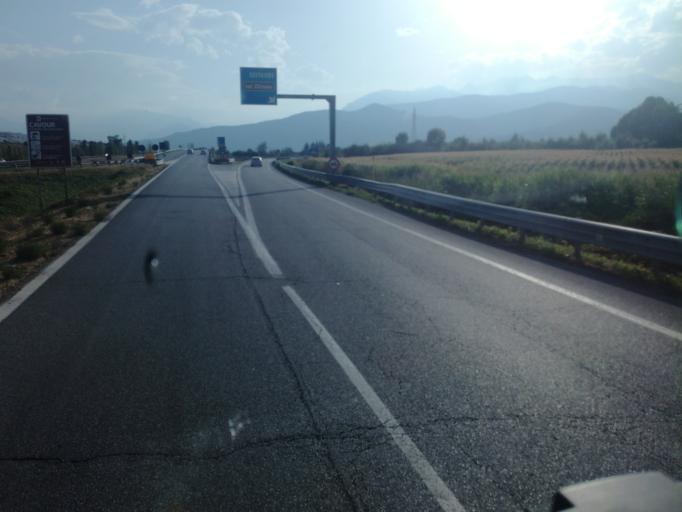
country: IT
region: Piedmont
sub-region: Provincia di Torino
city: Pinerolo
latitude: 44.8723
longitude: 7.3478
